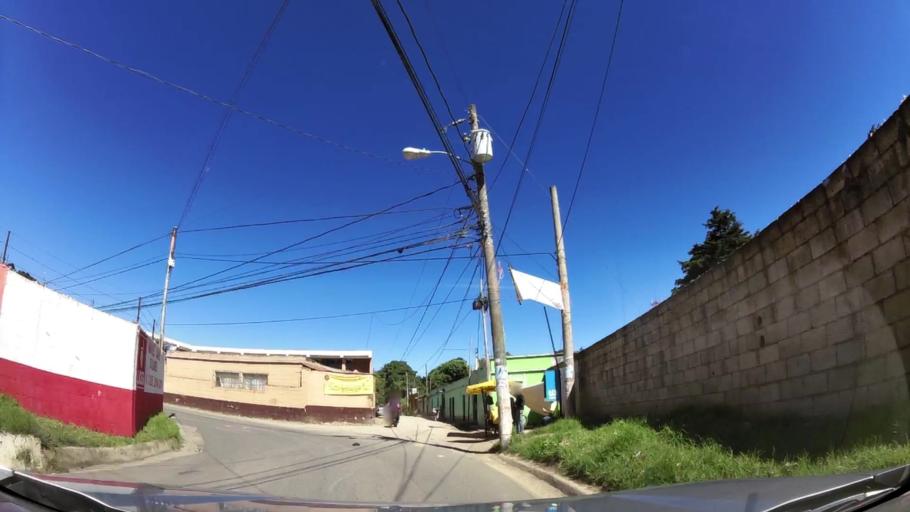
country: GT
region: Guatemala
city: San Jose Pinula
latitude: 14.5275
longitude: -90.4152
